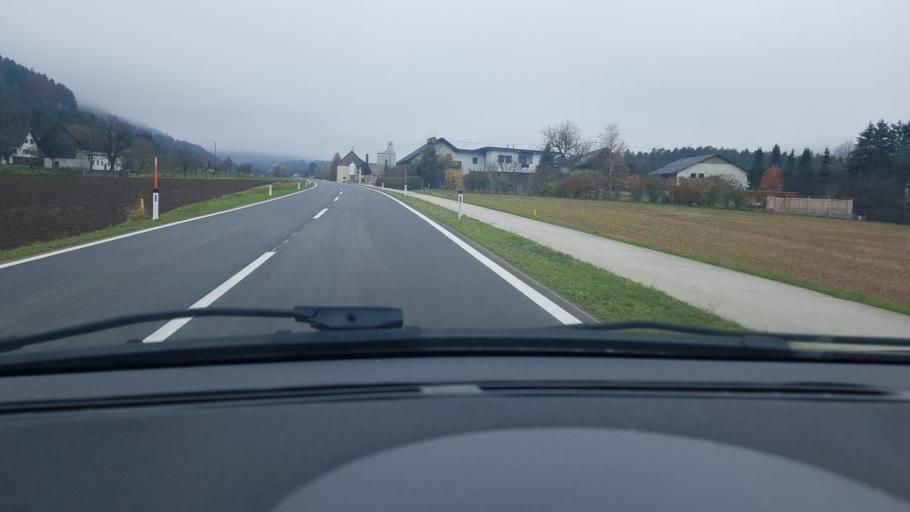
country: AT
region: Carinthia
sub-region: Politischer Bezirk Wolfsberg
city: Lavamund
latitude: 46.6466
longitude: 14.9206
